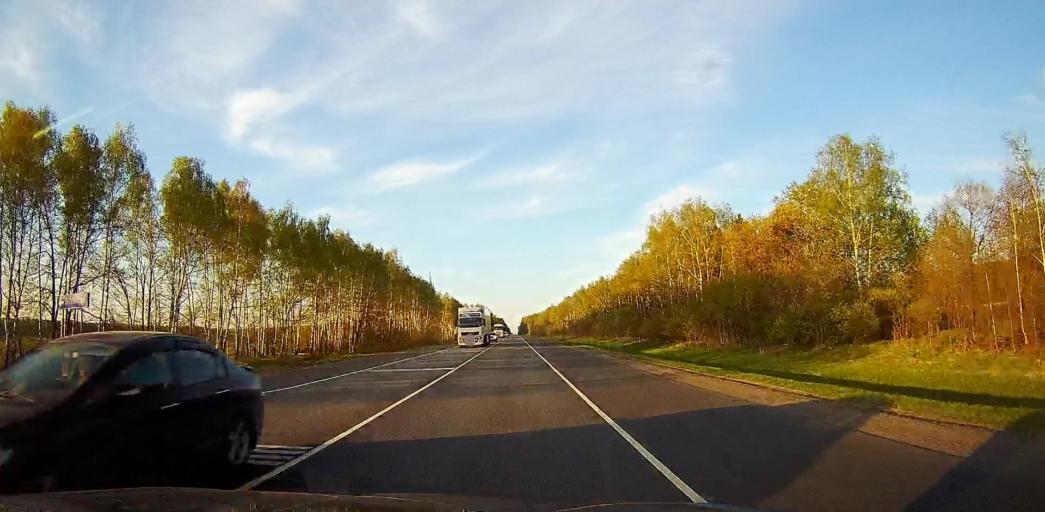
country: RU
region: Moskovskaya
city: Meshcherino
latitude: 55.2437
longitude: 38.4344
